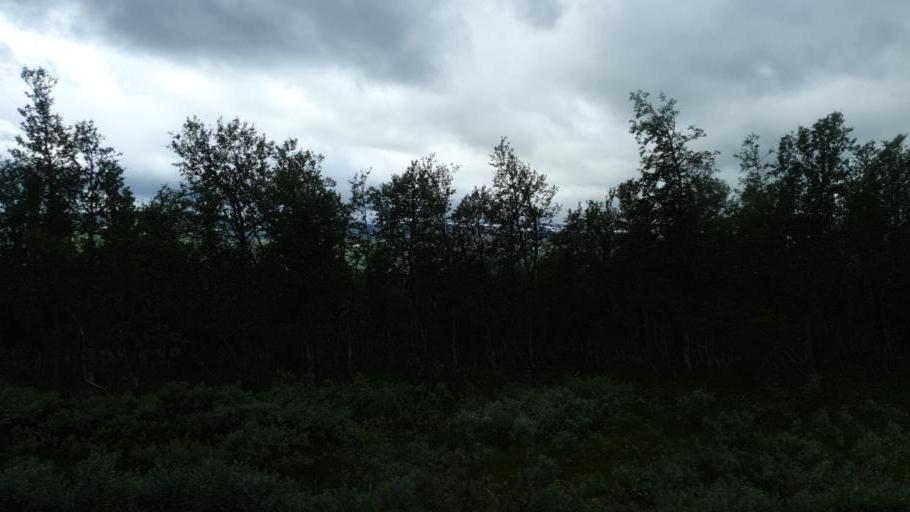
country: NO
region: Oppland
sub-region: Vestre Slidre
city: Slidre
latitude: 61.2676
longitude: 8.8645
